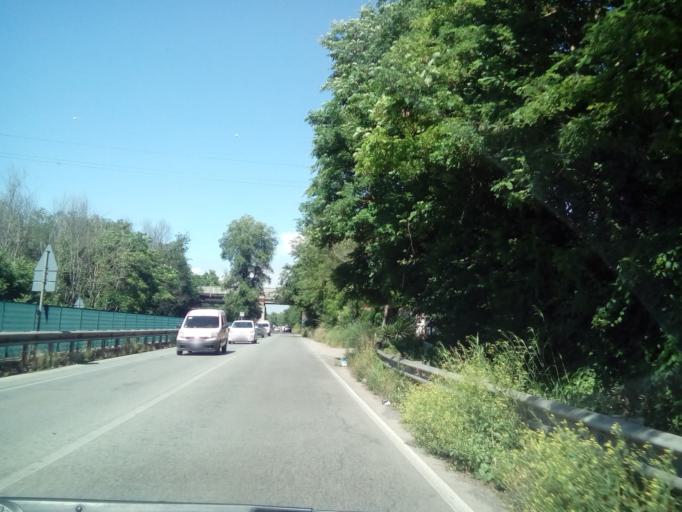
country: IT
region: Latium
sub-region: Citta metropolitana di Roma Capitale
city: Vitinia
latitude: 41.8349
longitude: 12.4564
